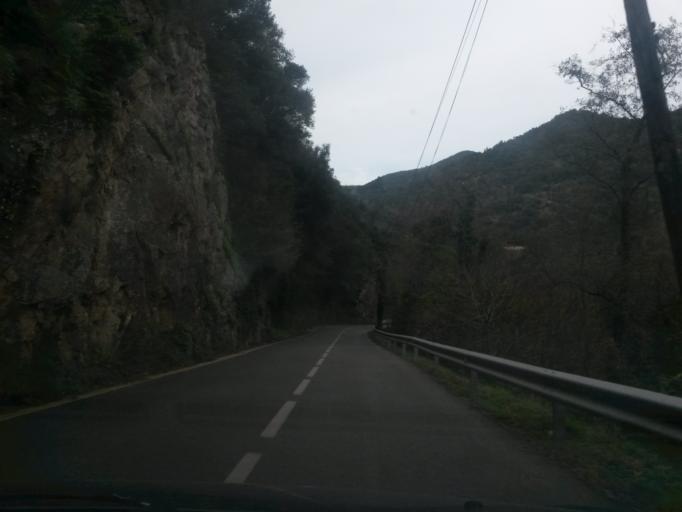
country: ES
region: Catalonia
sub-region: Provincia de Girona
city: la Cellera de Ter
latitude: 41.9497
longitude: 2.6117
